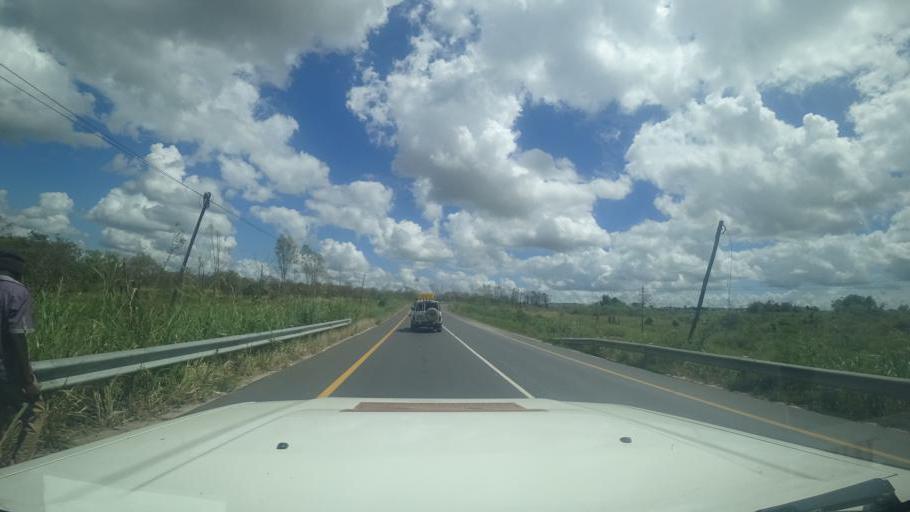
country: MZ
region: Sofala
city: Dondo
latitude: -19.5734
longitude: 34.7059
